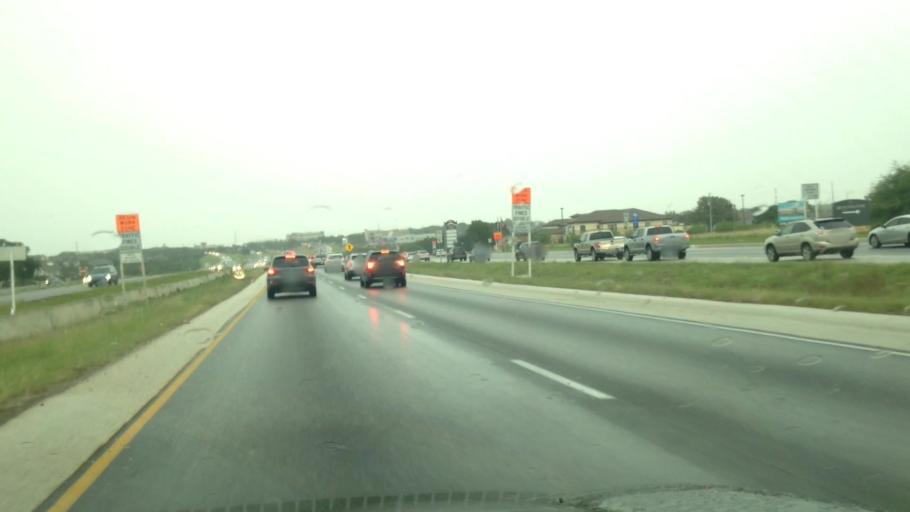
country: US
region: Texas
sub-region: Bexar County
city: Shavano Park
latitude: 29.6008
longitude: -98.5476
